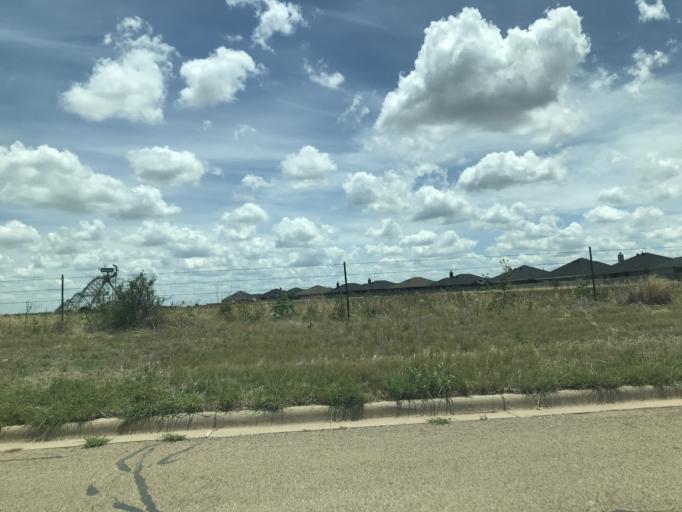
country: US
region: Texas
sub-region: Taylor County
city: Abilene
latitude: 32.4903
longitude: -99.6850
